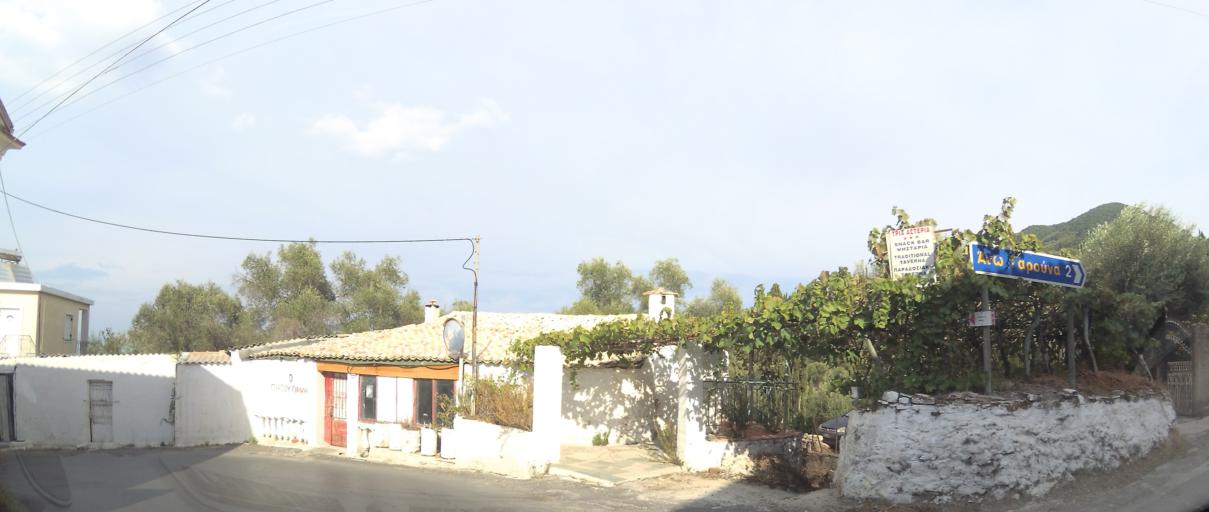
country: GR
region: Ionian Islands
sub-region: Nomos Kerkyras
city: Kynopiastes
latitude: 39.5528
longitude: 19.8627
